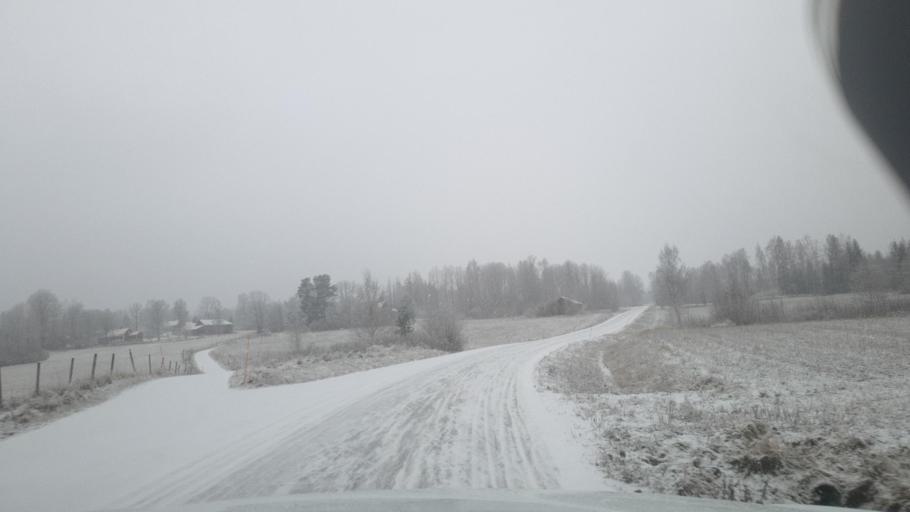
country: SE
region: Vaermland
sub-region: Grums Kommun
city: Slottsbron
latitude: 59.4604
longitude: 12.8772
